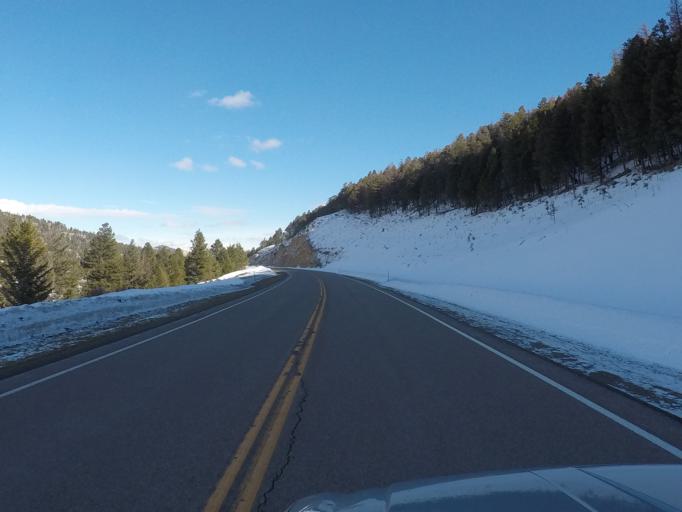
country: US
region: Montana
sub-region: Meagher County
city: White Sulphur Springs
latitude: 46.5558
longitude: -110.5021
